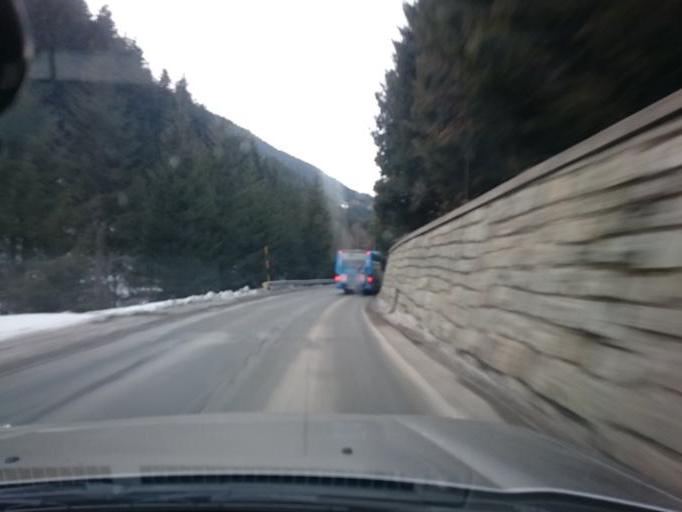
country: IT
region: Lombardy
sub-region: Provincia di Sondrio
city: Sant'Antonio
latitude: 46.4401
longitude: 10.4486
